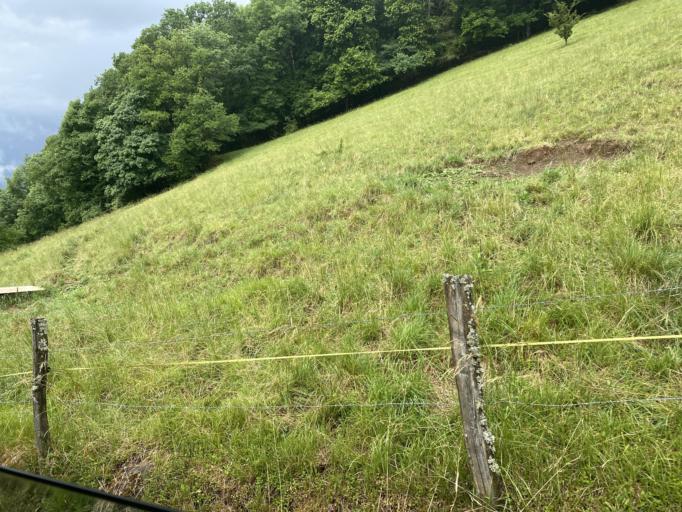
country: CH
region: Vaud
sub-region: Aigle District
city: Leysin
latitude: 46.3263
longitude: 7.0005
